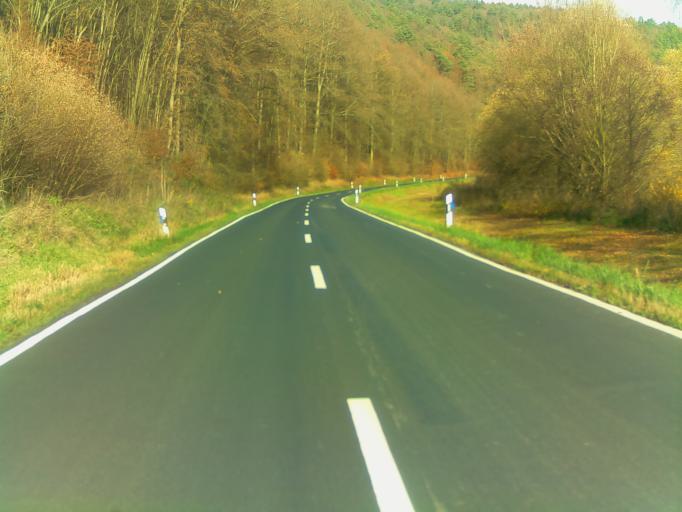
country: DE
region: Bavaria
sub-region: Regierungsbezirk Unterfranken
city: Bad Bocklet
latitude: 50.2928
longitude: 10.1001
